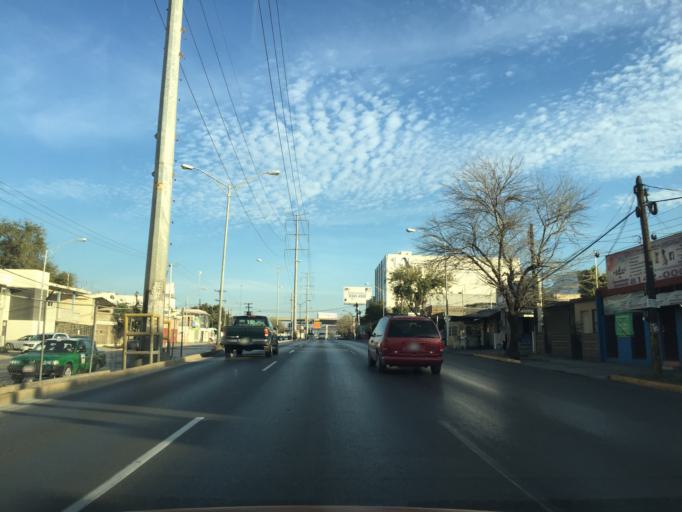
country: MX
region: Nuevo Leon
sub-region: San Nicolas de los Garza
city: San Nicolas de los Garza
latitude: 25.7131
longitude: -100.2803
